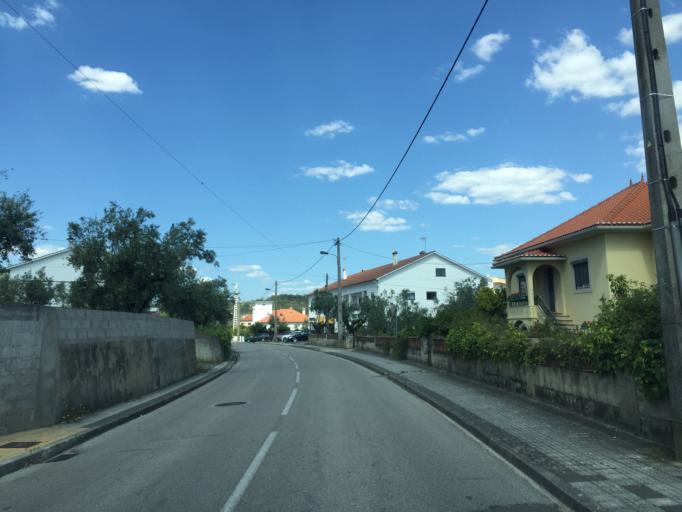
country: PT
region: Leiria
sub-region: Alvaiazere
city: Alvaiazere
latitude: 39.7583
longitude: -8.4611
